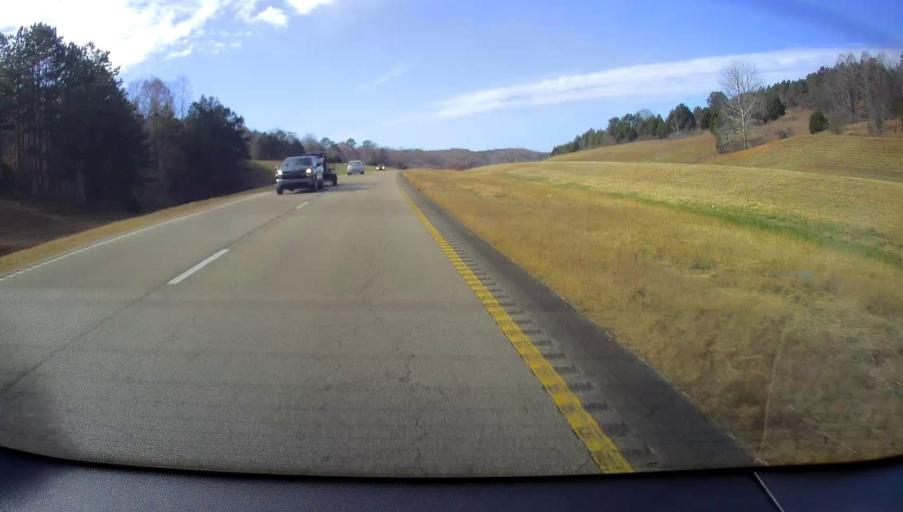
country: US
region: Mississippi
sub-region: Alcorn County
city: Corinth
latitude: 34.9317
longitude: -88.7605
